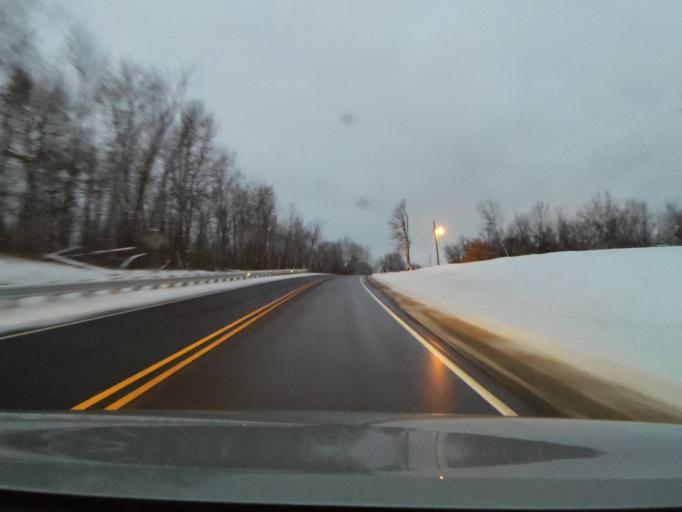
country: US
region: Wisconsin
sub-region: Dunn County
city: Menomonie
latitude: 44.9277
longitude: -91.9859
